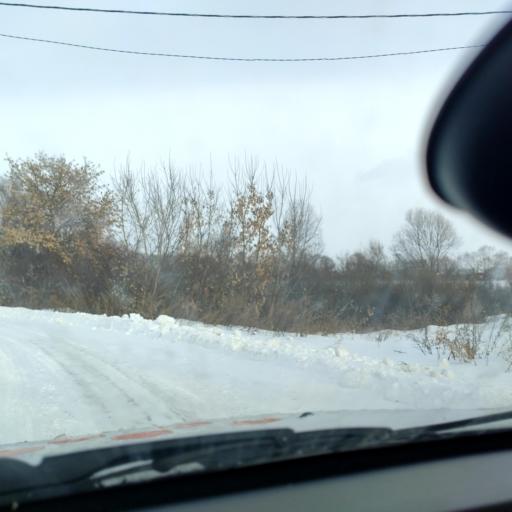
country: RU
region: Bashkortostan
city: Mikhaylovka
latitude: 54.8670
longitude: 55.7525
